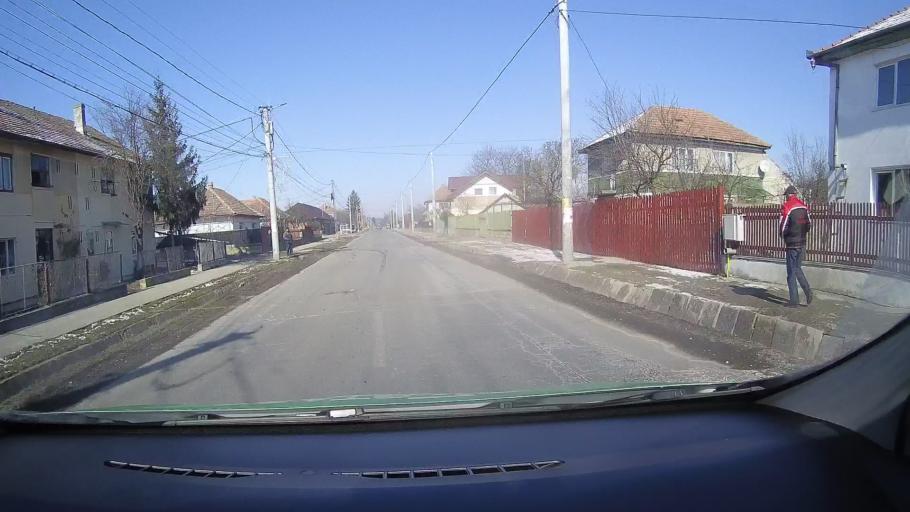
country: RO
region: Brasov
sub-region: Comuna Ungra
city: Ungra
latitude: 46.0154
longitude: 25.2754
